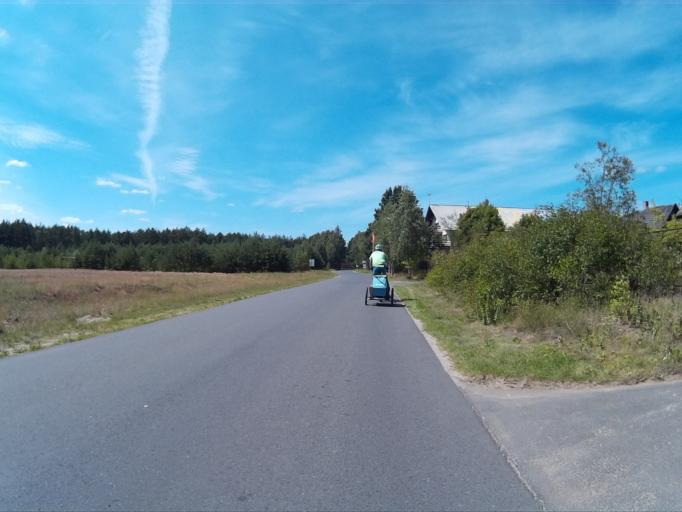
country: PL
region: Pomeranian Voivodeship
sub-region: Powiat chojnicki
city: Czersk
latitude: 53.7227
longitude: 17.9328
